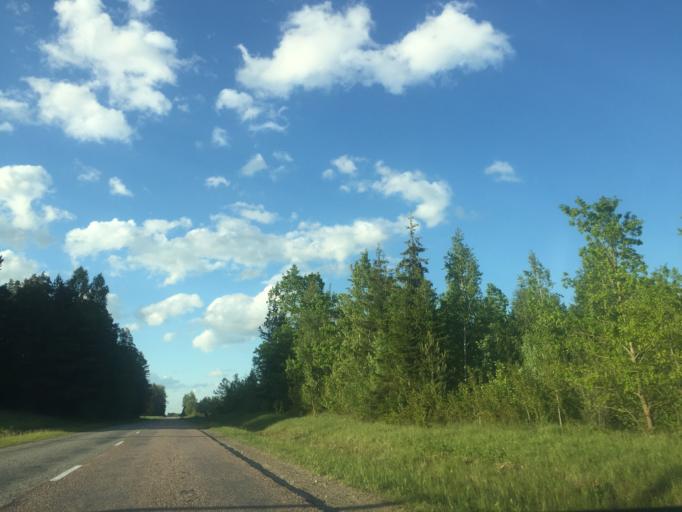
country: LV
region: Kandava
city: Kandava
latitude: 57.0102
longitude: 22.7846
